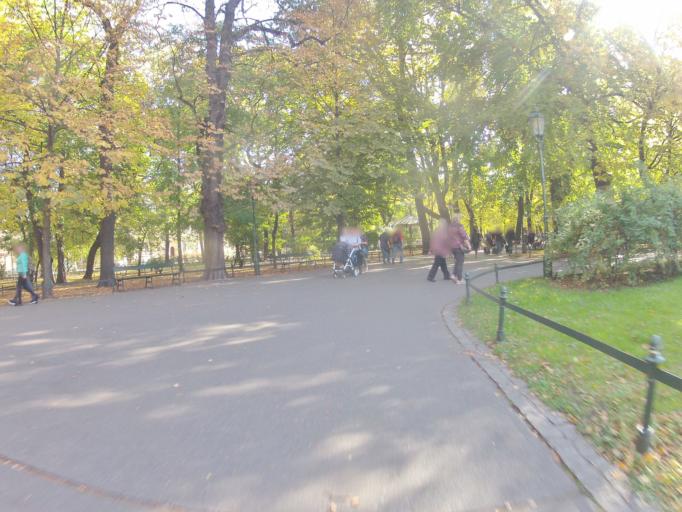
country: PL
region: Lesser Poland Voivodeship
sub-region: Krakow
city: Krakow
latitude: 50.0636
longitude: 19.9441
